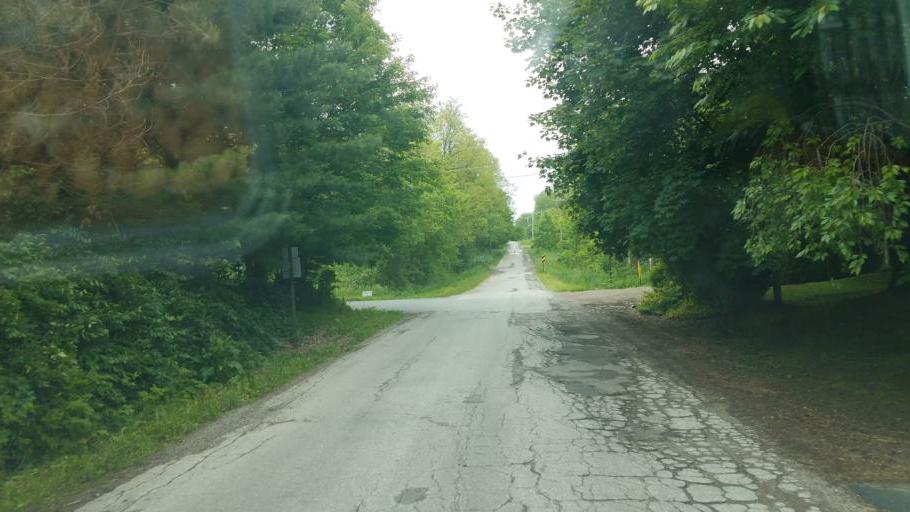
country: US
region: Ohio
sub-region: Knox County
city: Centerburg
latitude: 40.3760
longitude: -82.7237
